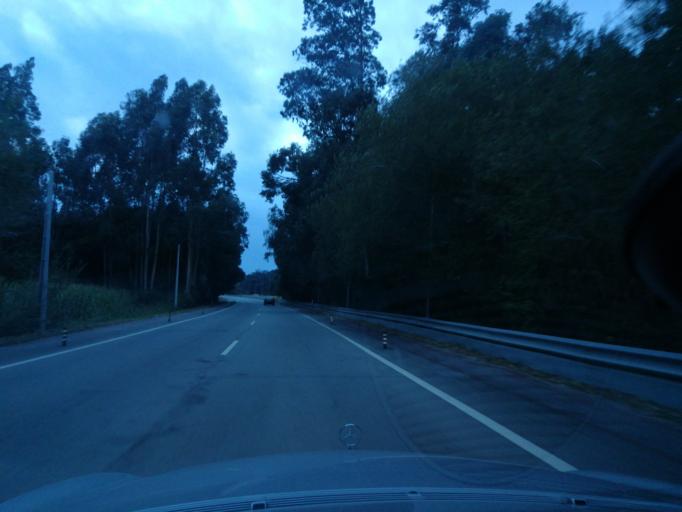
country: PT
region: Aveiro
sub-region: Murtosa
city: Murtosa
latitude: 40.7613
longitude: -8.6151
